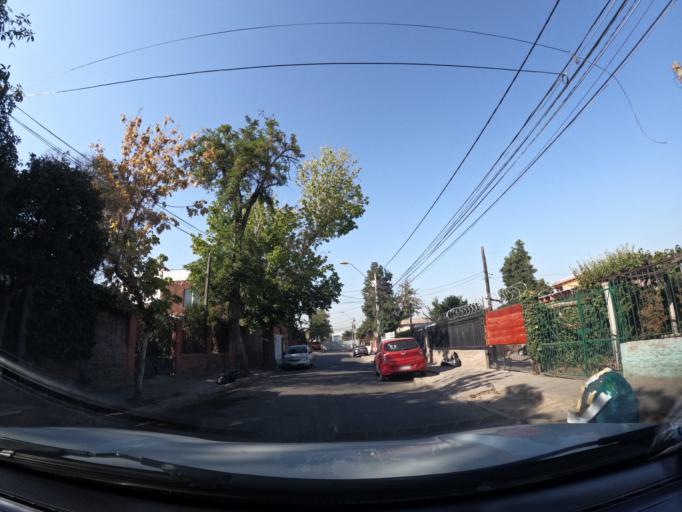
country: CL
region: Santiago Metropolitan
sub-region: Provincia de Santiago
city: Villa Presidente Frei, Nunoa, Santiago, Chile
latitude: -33.5059
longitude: -70.5711
